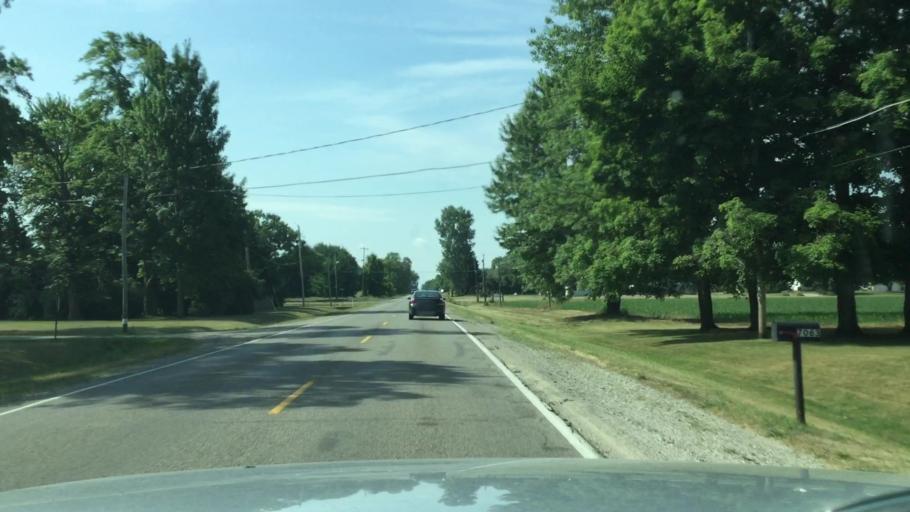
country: US
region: Michigan
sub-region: Genesee County
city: Flushing
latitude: 43.1054
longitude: -83.8137
